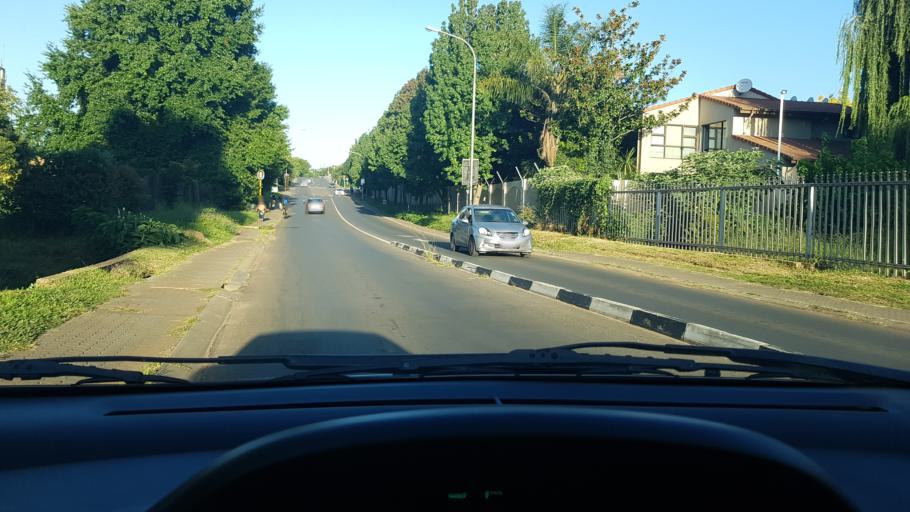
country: ZA
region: Gauteng
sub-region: Ekurhuleni Metropolitan Municipality
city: Germiston
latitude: -26.1798
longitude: 28.1302
